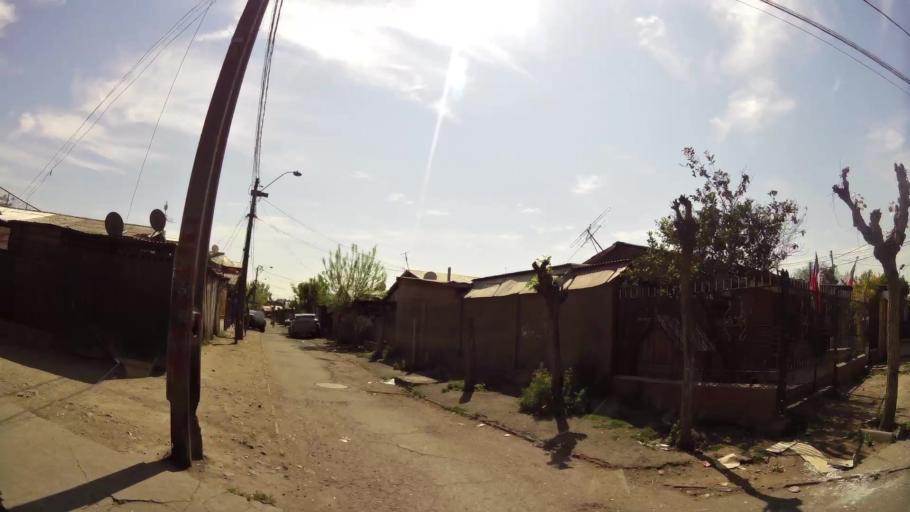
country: CL
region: Santiago Metropolitan
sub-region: Provincia de Santiago
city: La Pintana
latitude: -33.5620
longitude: -70.6451
